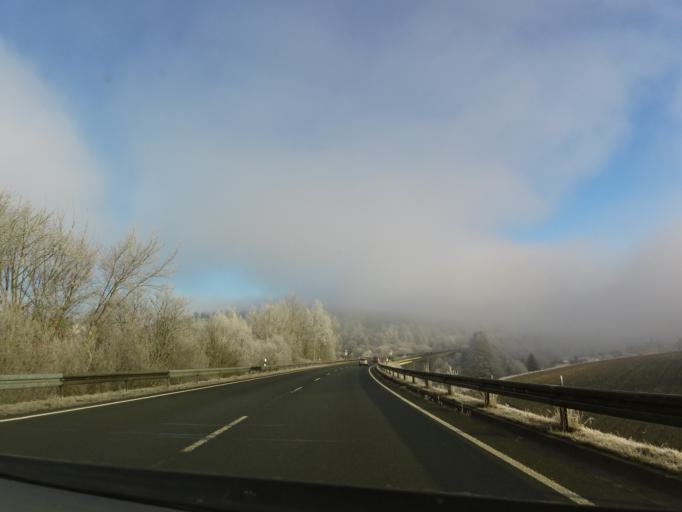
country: DE
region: Bavaria
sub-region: Upper Franconia
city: Arzberg
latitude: 50.0567
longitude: 12.1717
